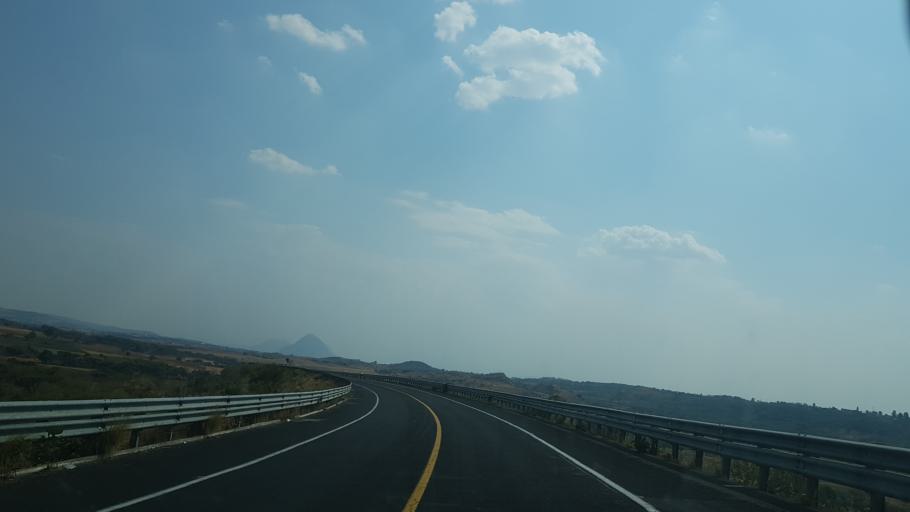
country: MX
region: Puebla
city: San Juan Amecac
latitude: 18.8181
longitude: -98.6944
